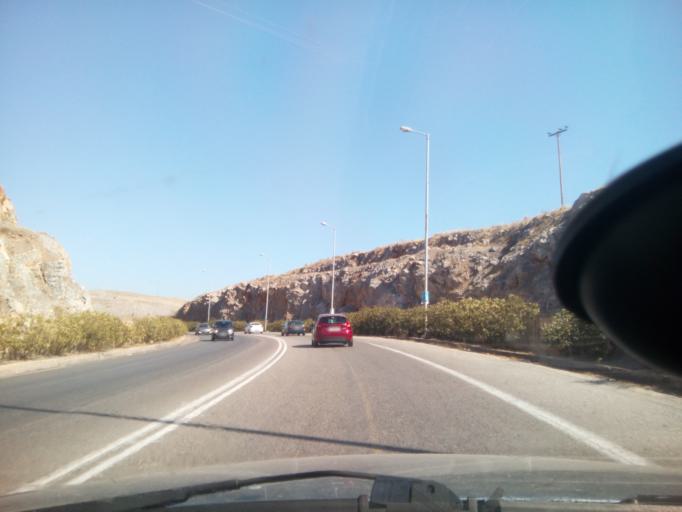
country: GR
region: Central Greece
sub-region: Nomos Evvoias
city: Chalkida
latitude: 38.4516
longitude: 23.6029
